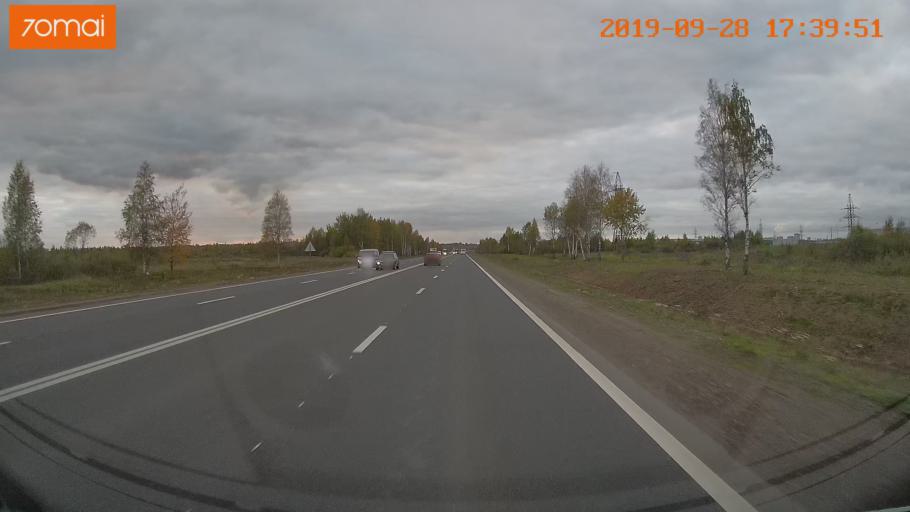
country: RU
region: Jaroslavl
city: Yaroslavl
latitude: 57.5469
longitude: 39.9092
